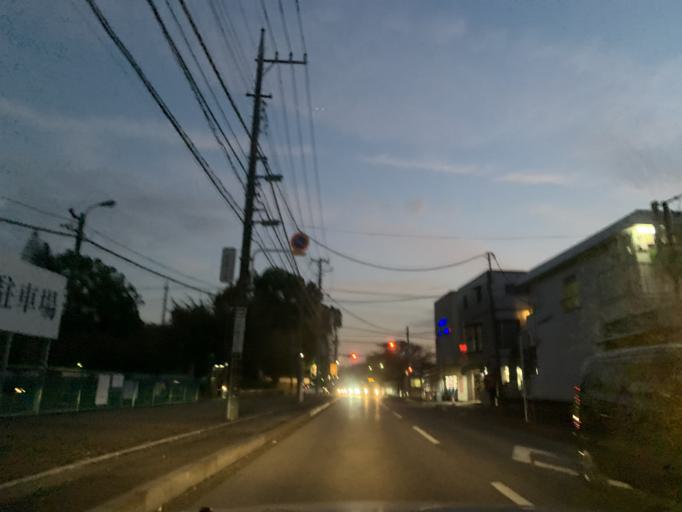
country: JP
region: Chiba
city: Noda
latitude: 35.9235
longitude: 139.9074
